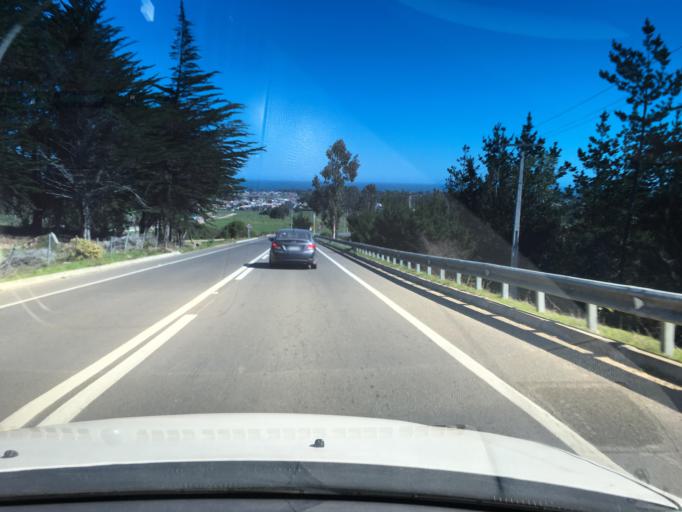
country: CL
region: Valparaiso
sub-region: San Antonio Province
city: El Tabo
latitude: -33.4227
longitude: -71.6834
